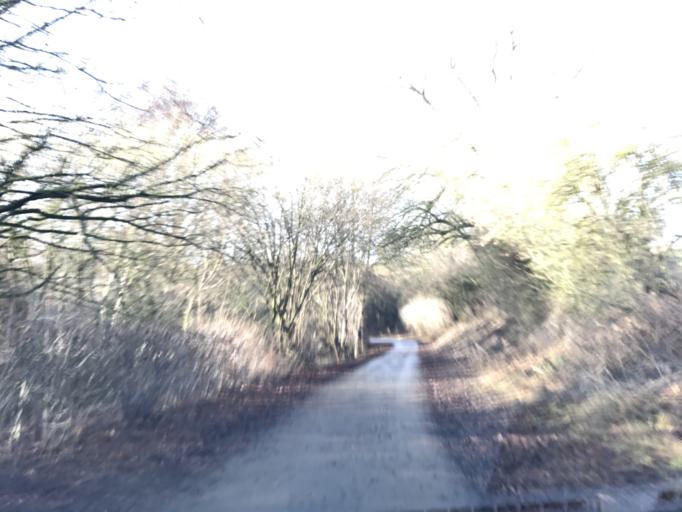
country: DE
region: Hesse
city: Trendelburg
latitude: 51.5798
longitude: 9.4028
